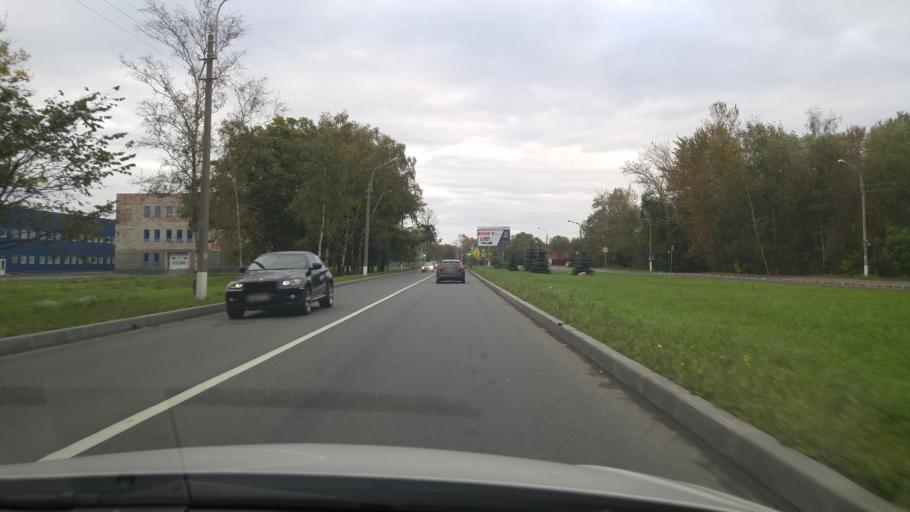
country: RU
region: St.-Petersburg
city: Kronshtadt
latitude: 60.0074
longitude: 29.7384
